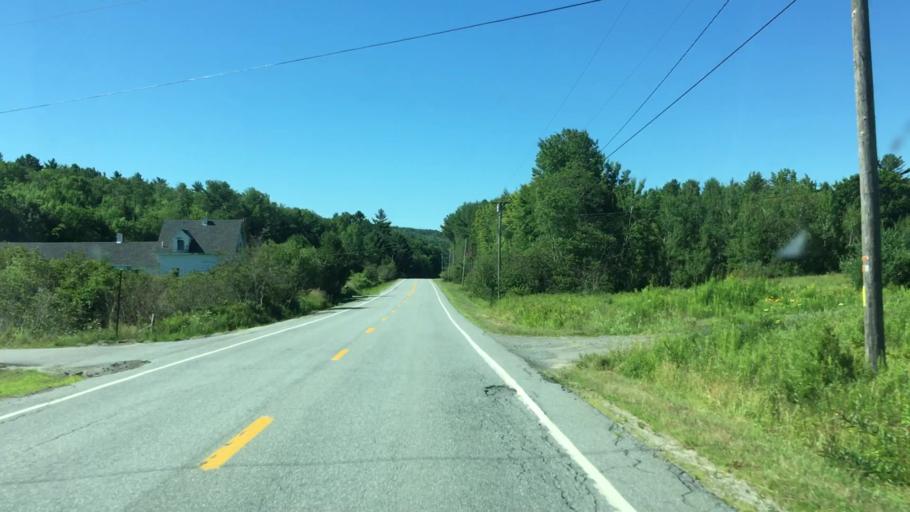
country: US
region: Maine
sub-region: Hancock County
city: Dedham
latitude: 44.6708
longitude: -68.6729
